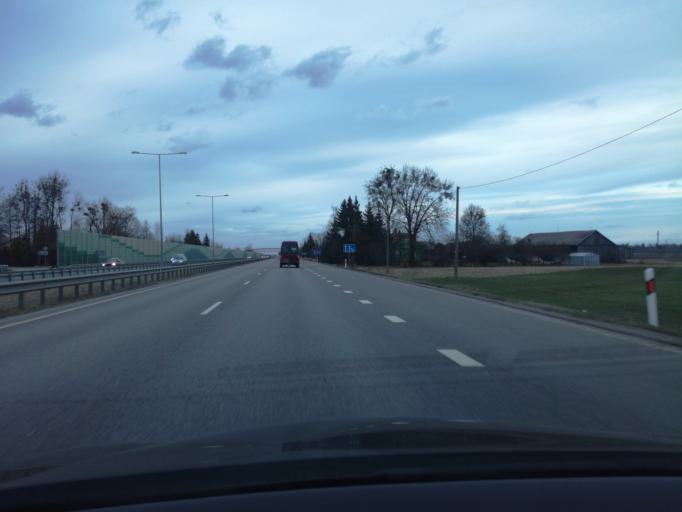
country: LT
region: Kauno apskritis
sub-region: Kauno rajonas
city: Mastaiciai
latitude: 54.7895
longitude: 23.7971
